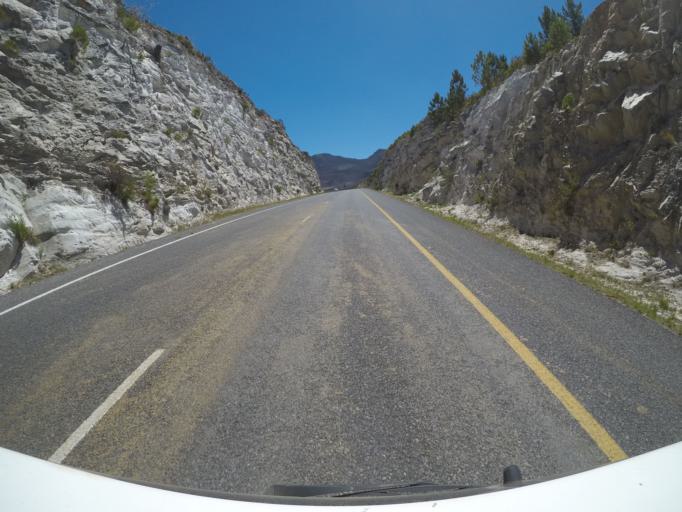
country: ZA
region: Western Cape
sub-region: Overberg District Municipality
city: Grabouw
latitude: -34.2194
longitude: 19.1739
